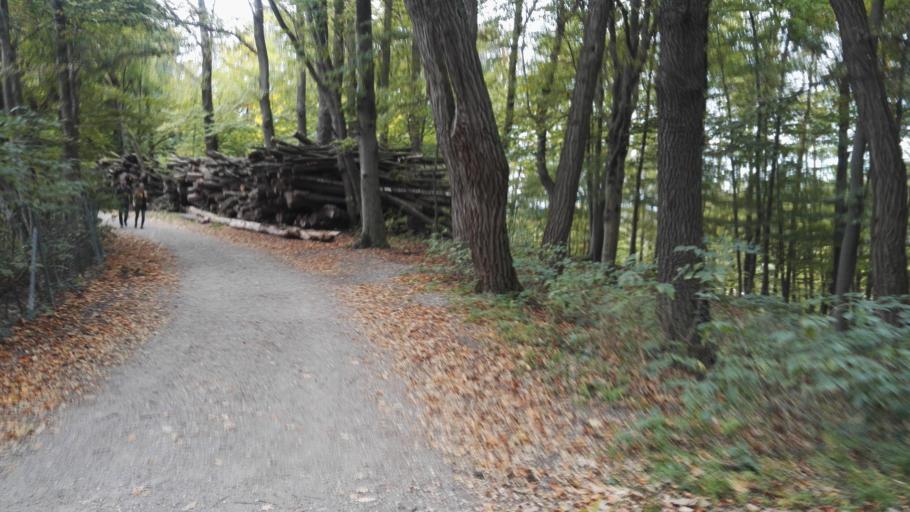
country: AT
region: Styria
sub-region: Graz Stadt
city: Mariatrost
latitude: 47.0981
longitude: 15.4881
